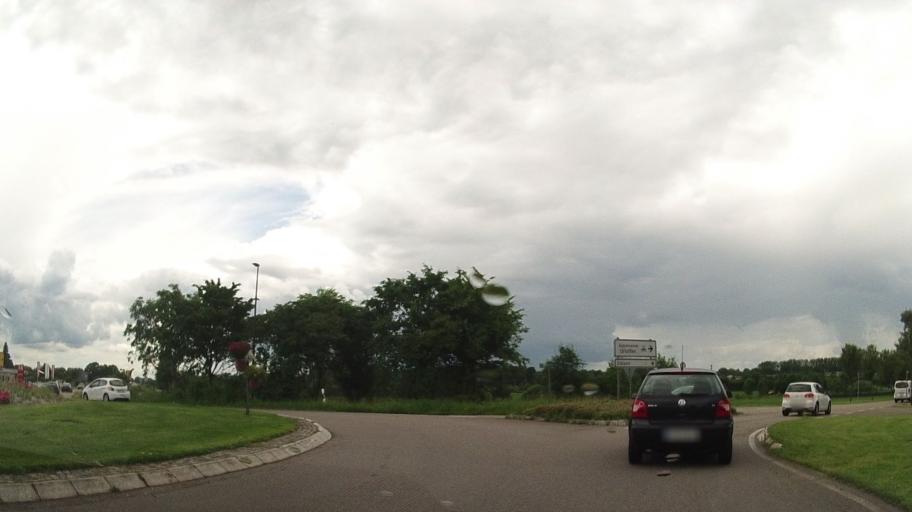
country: DE
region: Baden-Wuerttemberg
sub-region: Freiburg Region
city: Appenweier
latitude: 48.5340
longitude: 7.9758
